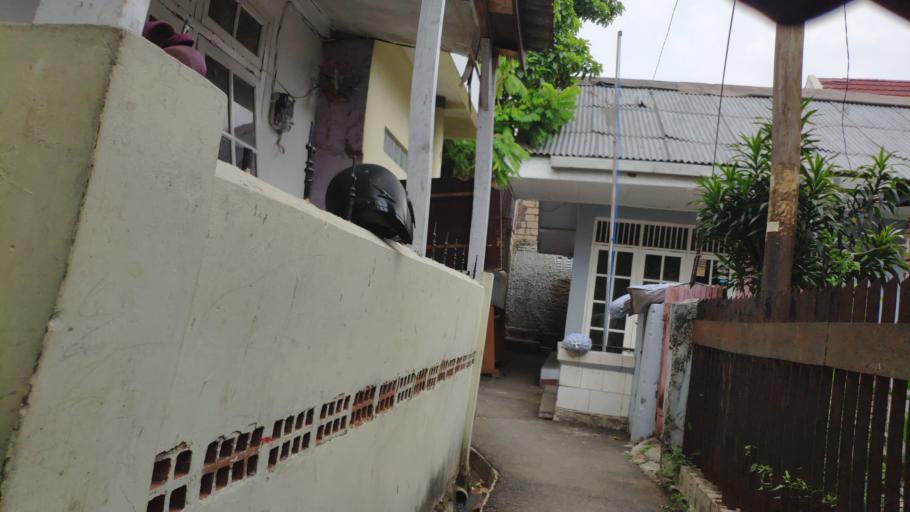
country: ID
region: Jakarta Raya
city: Jakarta
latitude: -6.2646
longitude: 106.7949
